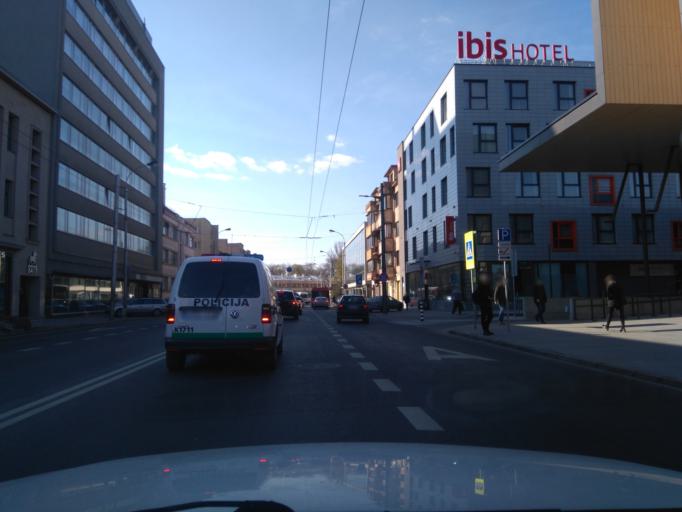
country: LT
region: Kauno apskritis
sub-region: Kaunas
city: Aleksotas
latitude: 54.8891
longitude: 23.9274
